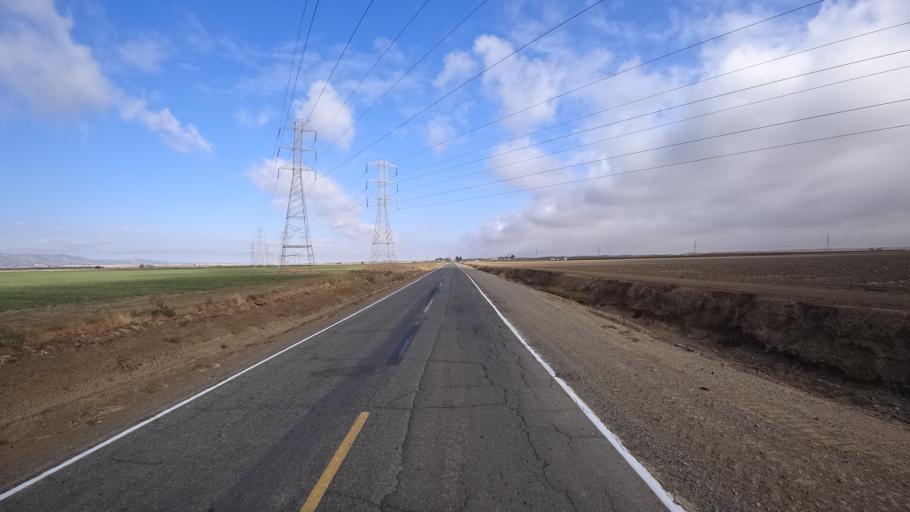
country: US
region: California
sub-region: Yolo County
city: Esparto
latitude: 38.7685
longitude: -122.0071
